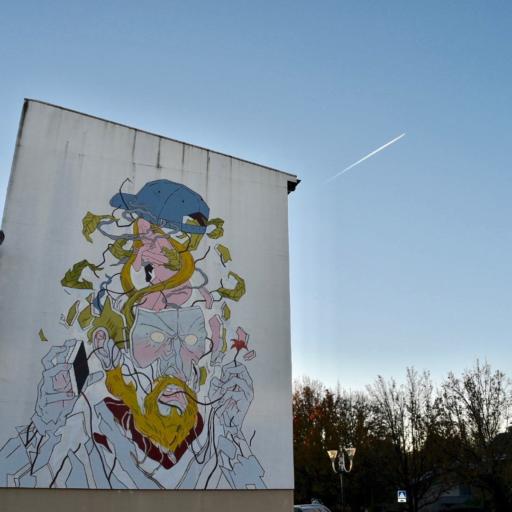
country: FR
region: Aquitaine
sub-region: Departement des Pyrenees-Atlantiques
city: Bayonne
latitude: 43.5032
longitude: -1.4697
